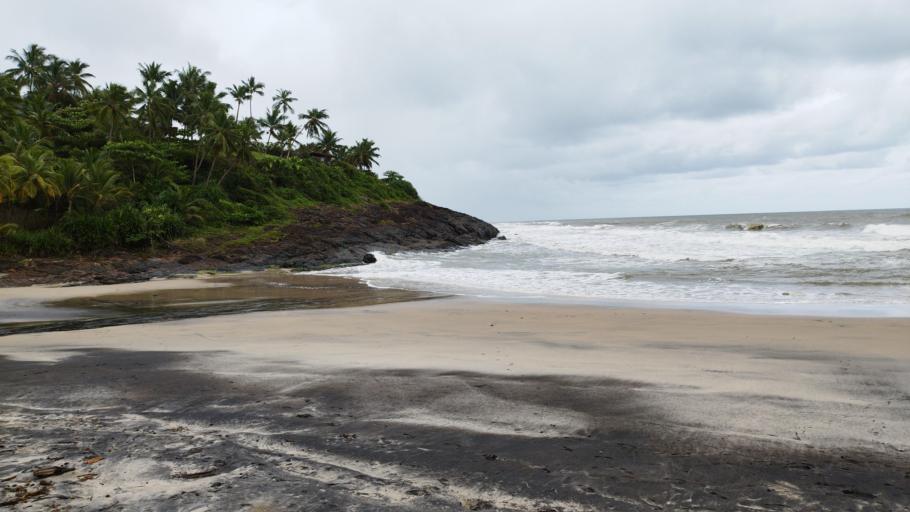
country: BR
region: Bahia
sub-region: Itacare
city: Itacare
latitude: -14.2888
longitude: -38.9854
